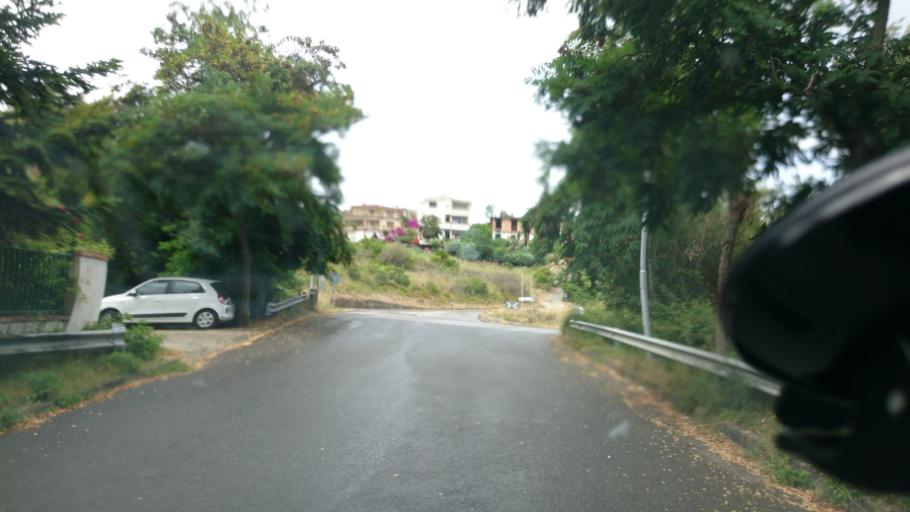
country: IT
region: Campania
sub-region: Provincia di Salerno
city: Palinuro
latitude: 40.0301
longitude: 15.2860
